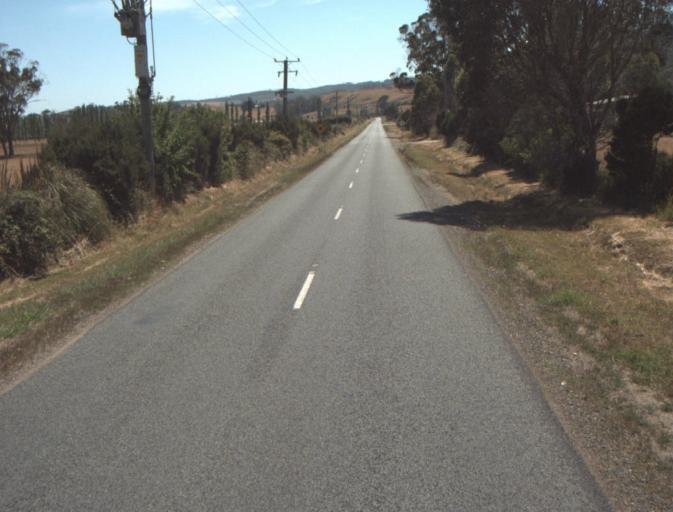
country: AU
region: Tasmania
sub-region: Launceston
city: Mayfield
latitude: -41.2561
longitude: 147.1464
